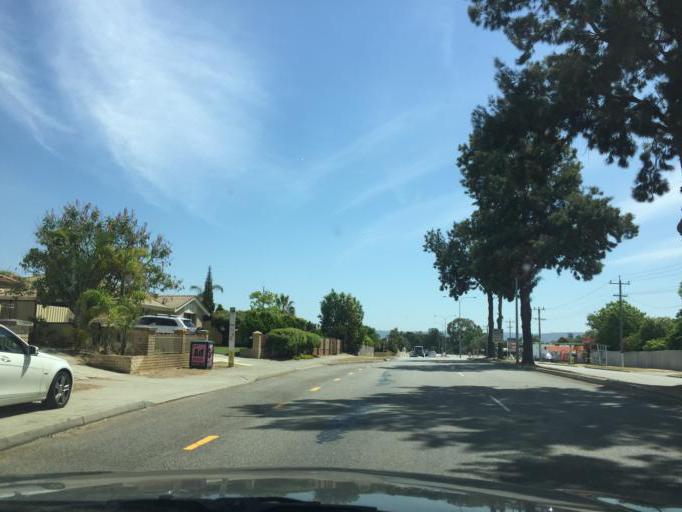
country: AU
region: Western Australia
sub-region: Gosnells
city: Thornlie
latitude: -32.0724
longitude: 115.9646
